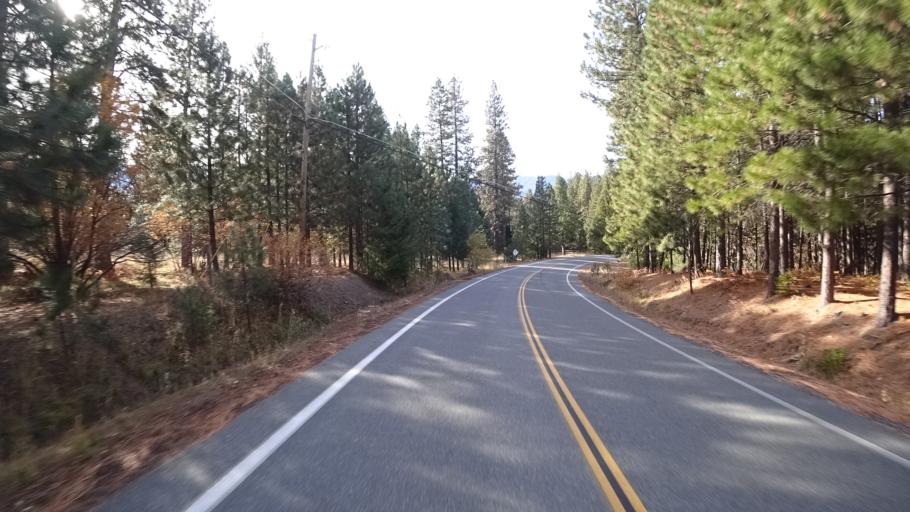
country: US
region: California
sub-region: Siskiyou County
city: Weed
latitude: 41.3969
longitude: -122.4168
